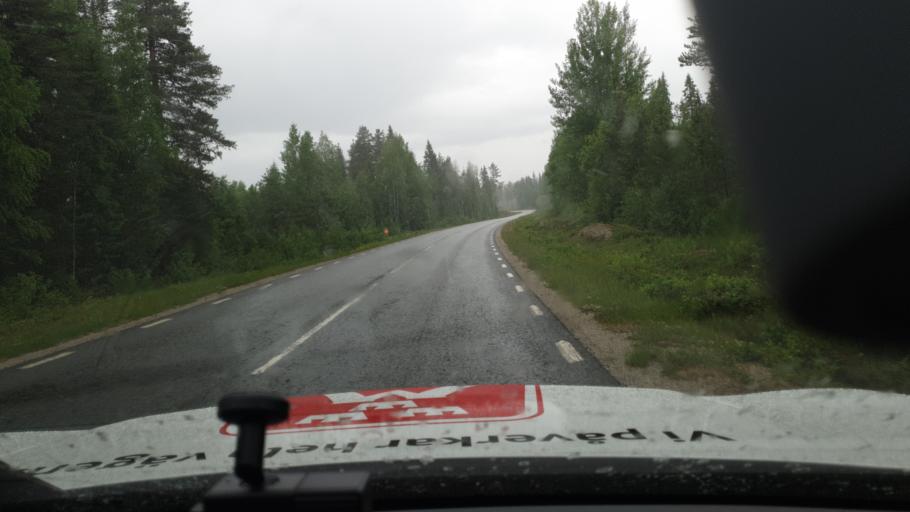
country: SE
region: Vaesterbotten
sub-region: Lycksele Kommun
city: Lycksele
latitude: 64.4437
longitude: 18.9423
